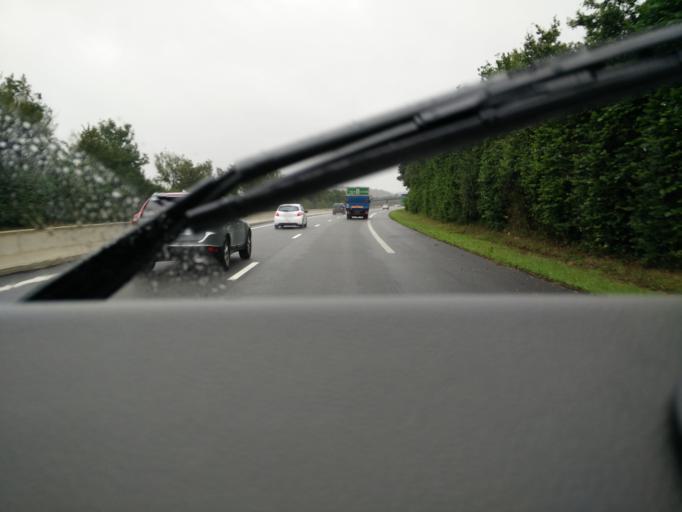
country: FR
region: Nord-Pas-de-Calais
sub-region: Departement du Pas-de-Calais
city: Saint-Pol-sur-Ternoise
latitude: 50.3732
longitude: 2.3011
